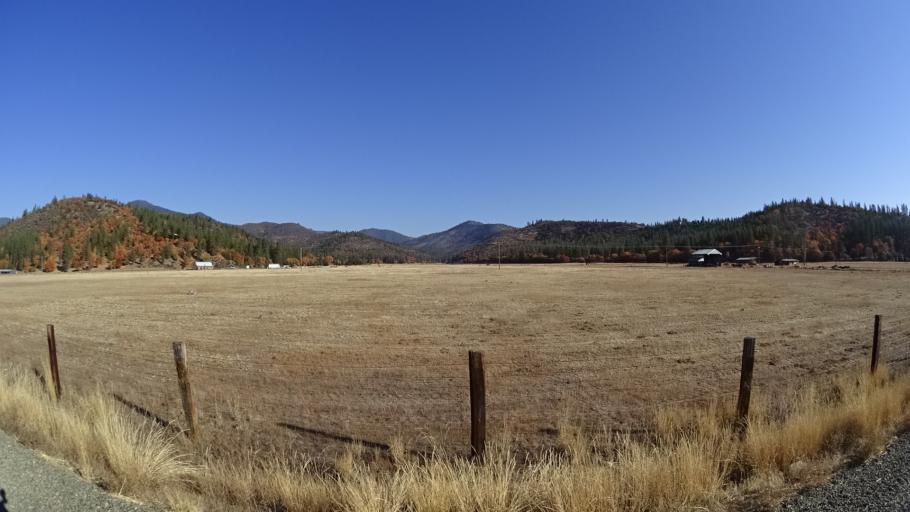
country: US
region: California
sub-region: Siskiyou County
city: Yreka
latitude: 41.6313
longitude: -122.8947
